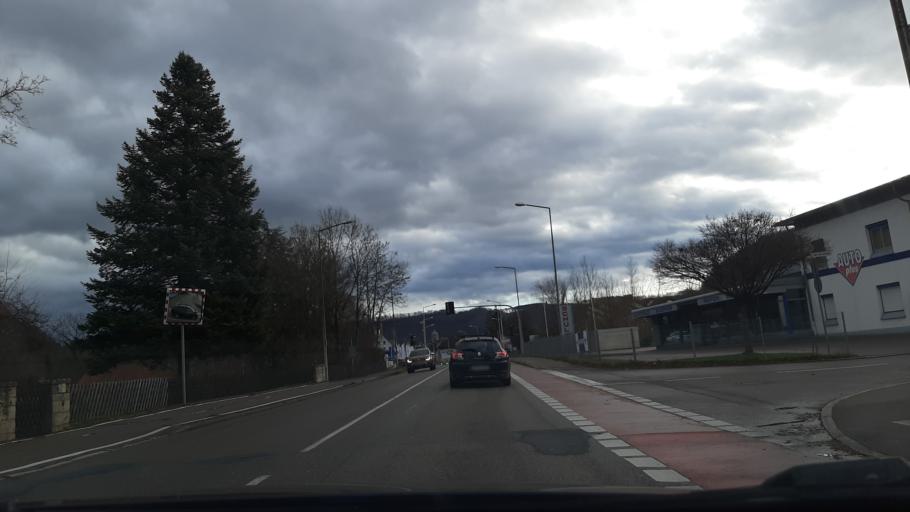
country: DE
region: Baden-Wuerttemberg
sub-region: Regierungsbezirk Stuttgart
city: Kuchen
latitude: 48.6298
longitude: 9.8122
